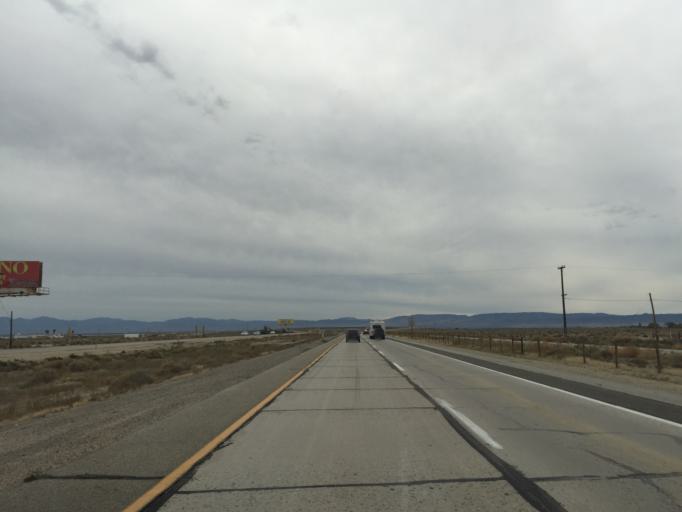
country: US
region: California
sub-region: Kern County
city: Rosamond
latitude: 34.8286
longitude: -118.1704
